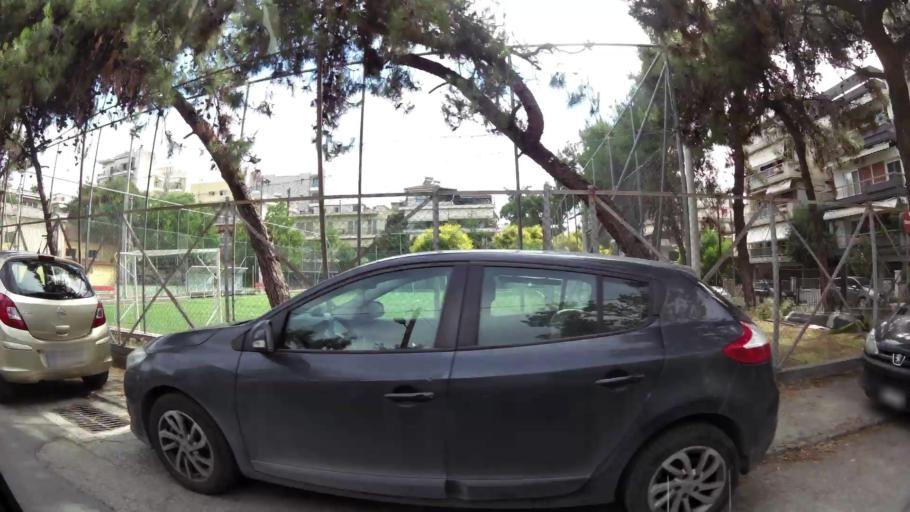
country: GR
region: Central Macedonia
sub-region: Nomos Thessalonikis
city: Kalamaria
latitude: 40.5810
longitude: 22.9483
